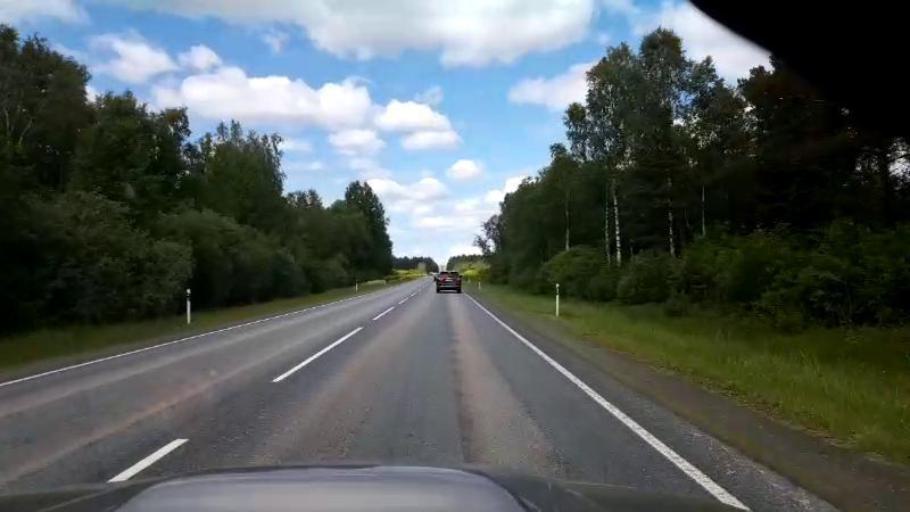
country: EE
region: Harju
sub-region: Saue linn
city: Saue
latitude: 59.1652
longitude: 24.5040
